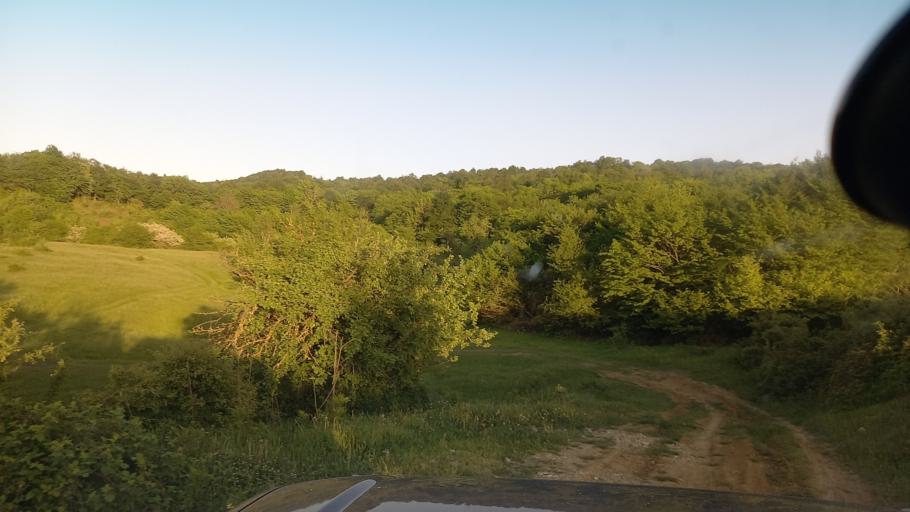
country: RU
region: Dagestan
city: Khuchni
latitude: 42.0072
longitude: 47.9717
